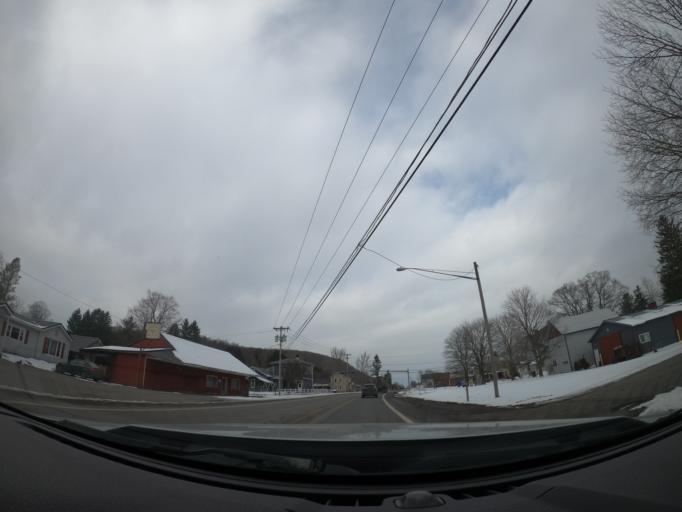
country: US
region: New York
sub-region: Cortland County
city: Homer
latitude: 42.7345
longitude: -76.1484
